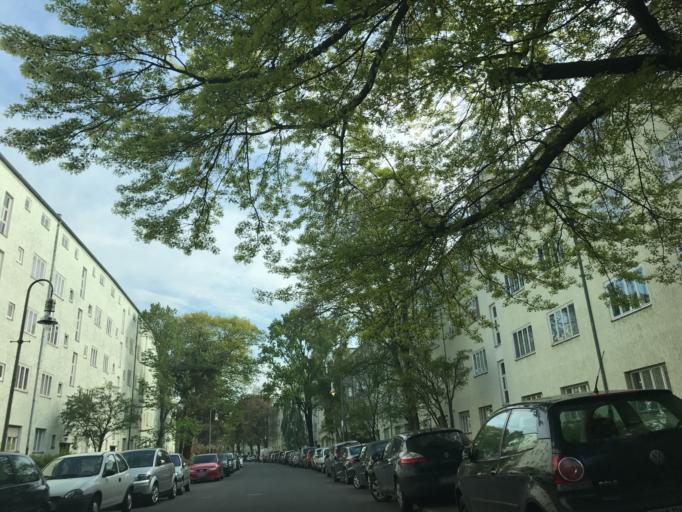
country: DE
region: Berlin
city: Siemensstadt
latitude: 52.5399
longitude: 13.2711
